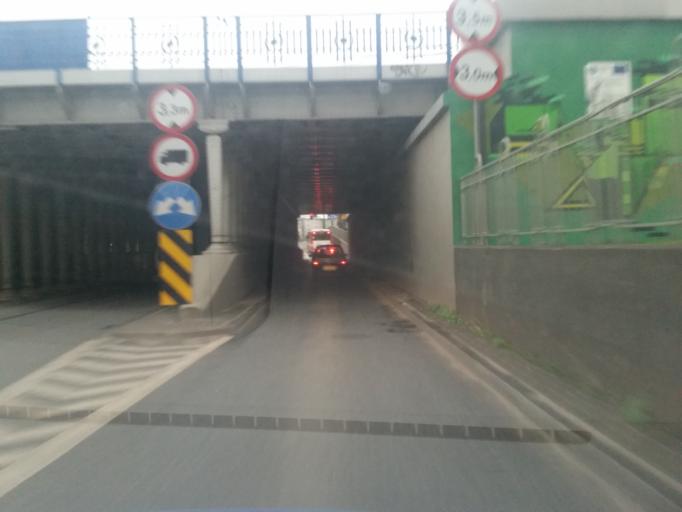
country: PL
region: Silesian Voivodeship
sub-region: Sosnowiec
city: Sosnowiec
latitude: 50.2767
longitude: 19.1210
